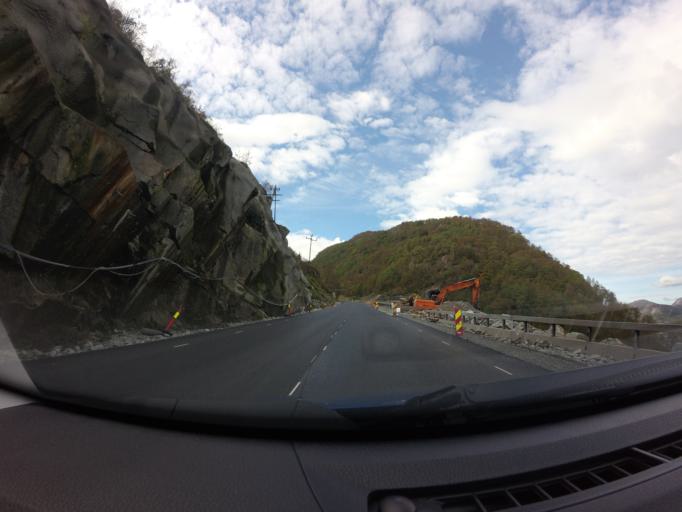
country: NO
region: Rogaland
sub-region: Forsand
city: Forsand
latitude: 58.8391
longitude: 6.1553
